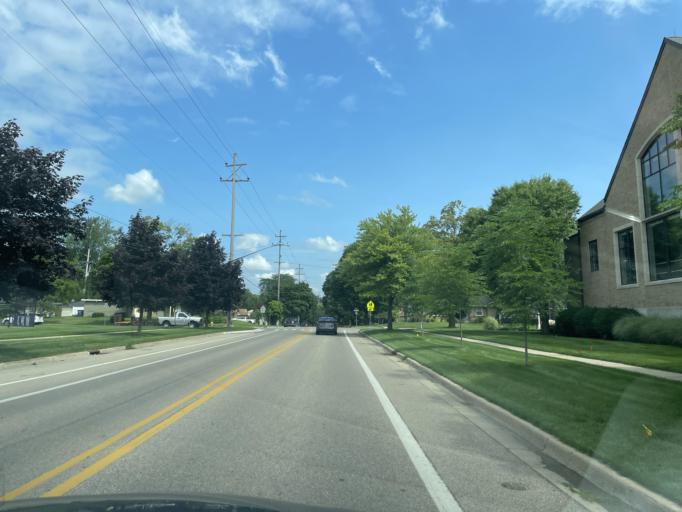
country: US
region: Michigan
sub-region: Kent County
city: East Grand Rapids
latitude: 42.9301
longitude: -85.6241
